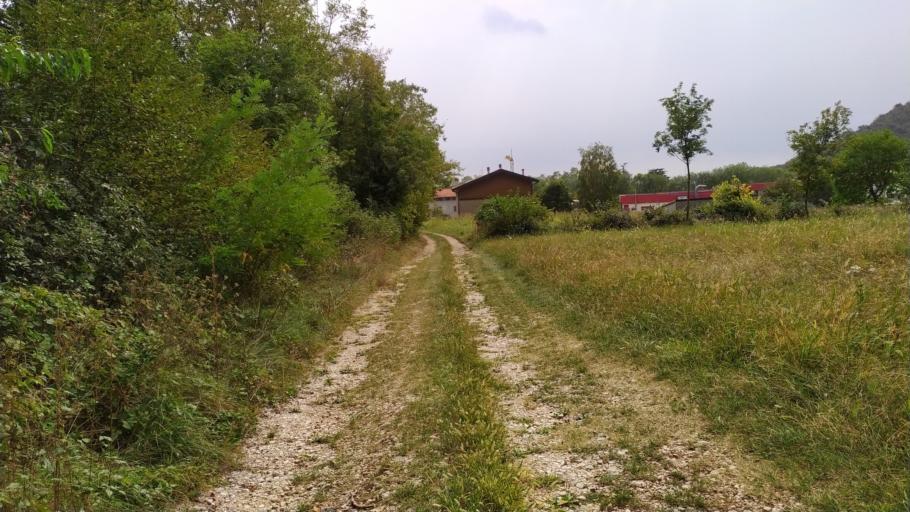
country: IT
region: Friuli Venezia Giulia
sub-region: Provincia di Pordenone
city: Aviano-Castello
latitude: 46.0818
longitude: 12.5750
